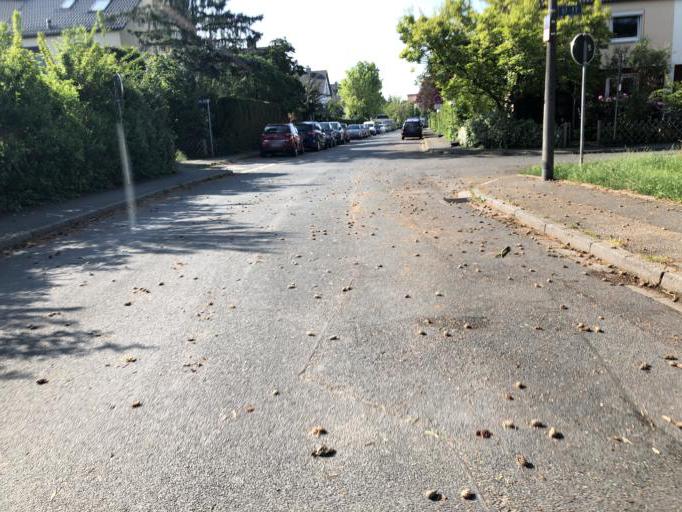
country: DE
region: Bavaria
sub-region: Regierungsbezirk Mittelfranken
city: Erlangen
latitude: 49.5549
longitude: 11.0208
